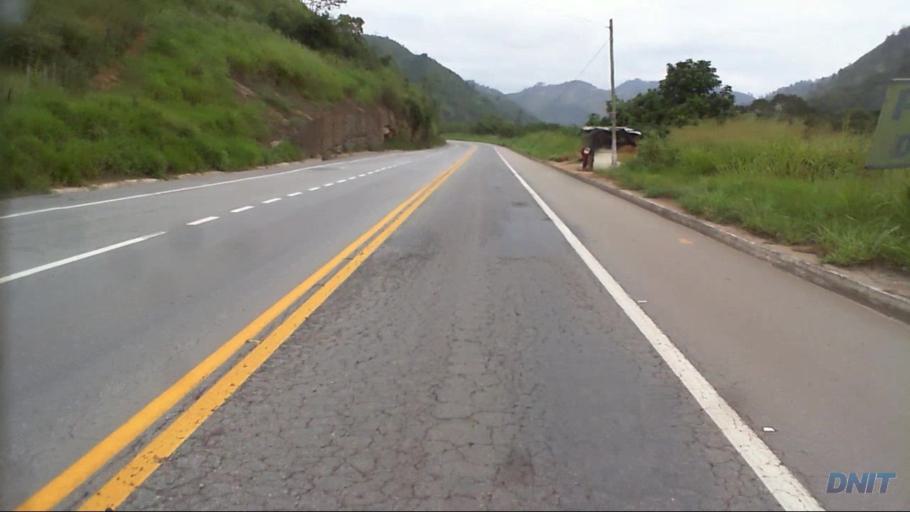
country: BR
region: Minas Gerais
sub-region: Timoteo
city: Timoteo
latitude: -19.5417
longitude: -42.6881
